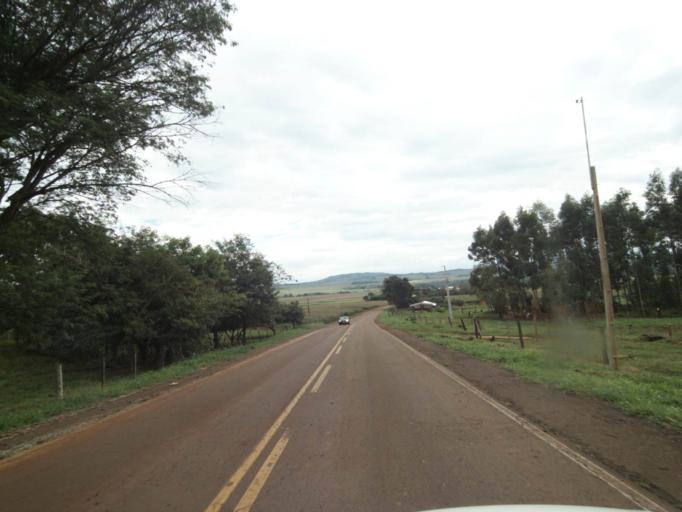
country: BR
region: Parana
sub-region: Marechal Candido Rondon
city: Marechal Candido Rondon
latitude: -24.7933
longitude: -54.2258
